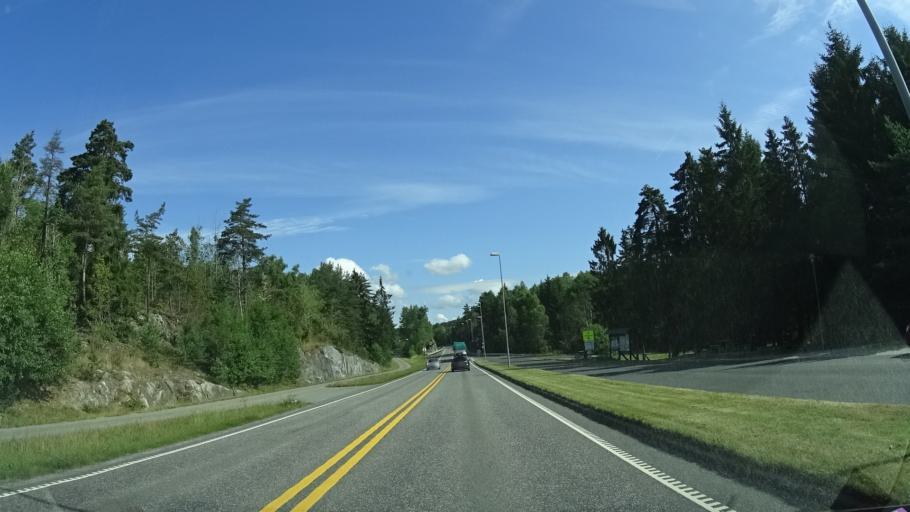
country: NO
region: Telemark
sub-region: Bamble
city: Langesund
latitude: 59.0235
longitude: 9.6779
